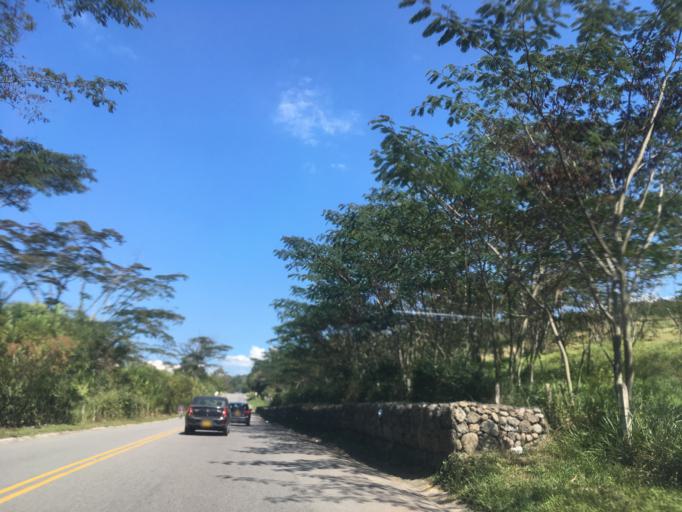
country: CO
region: Santander
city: Suaita
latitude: 6.0778
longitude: -73.3990
